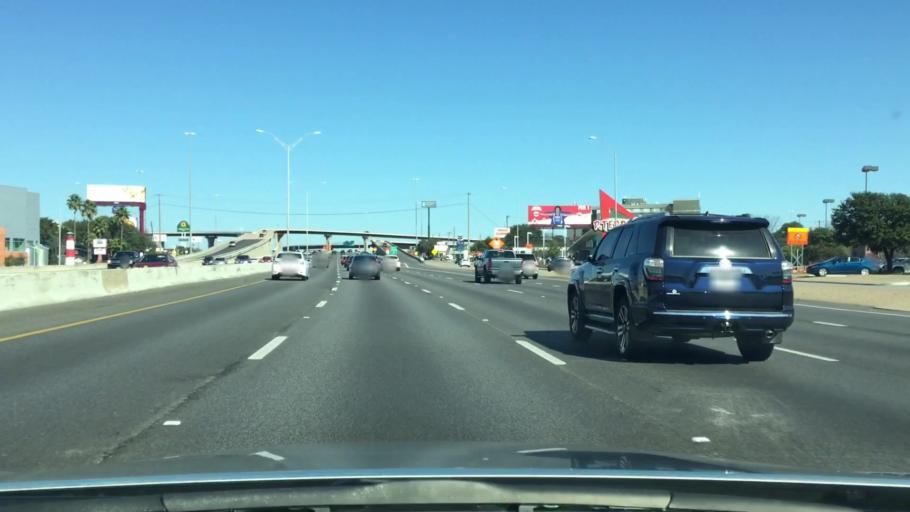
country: US
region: Texas
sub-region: Travis County
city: Austin
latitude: 30.3156
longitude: -97.7072
